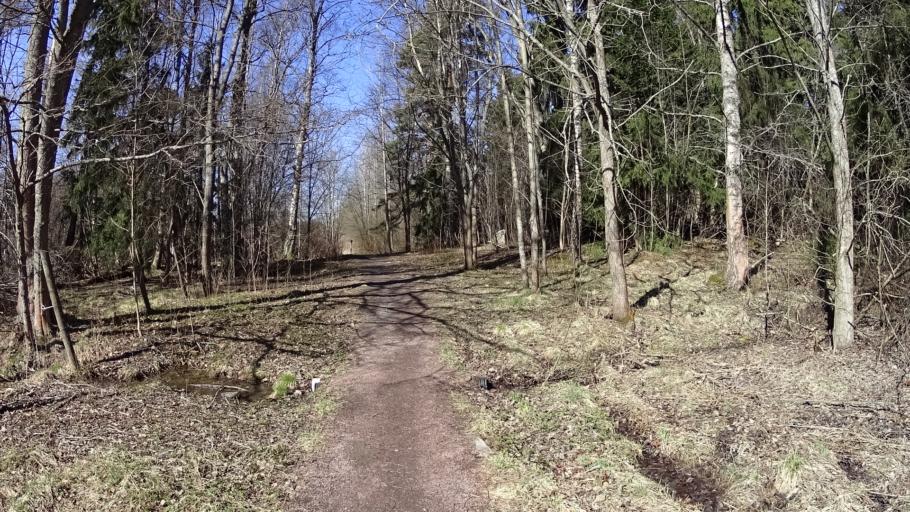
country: FI
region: Uusimaa
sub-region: Helsinki
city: Otaniemi
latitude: 60.2007
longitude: 24.8203
